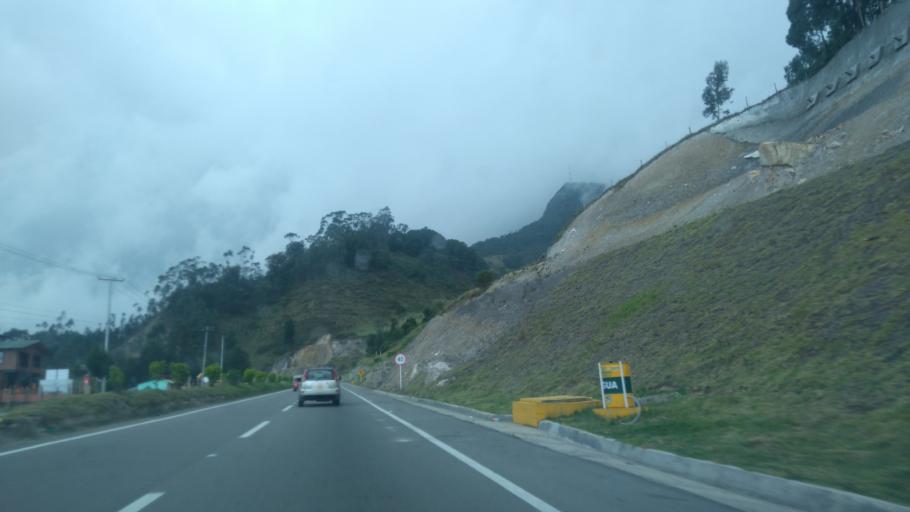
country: CO
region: Cundinamarca
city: El Rosal
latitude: 4.8933
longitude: -74.3063
